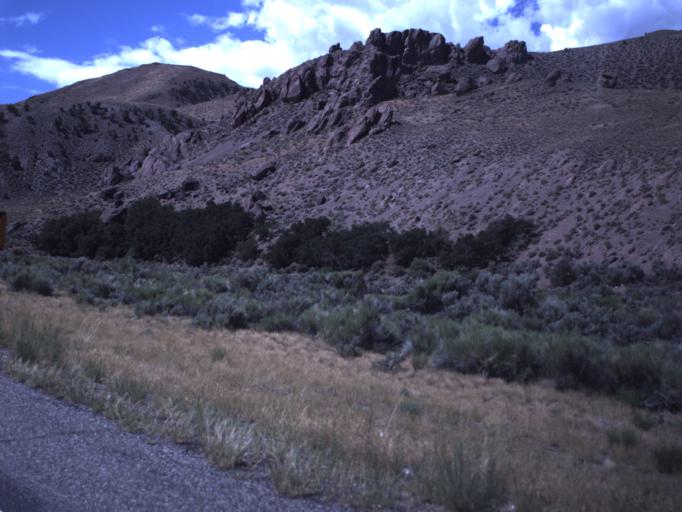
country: US
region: Utah
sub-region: Sevier County
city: Monroe
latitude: 38.4825
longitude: -112.2447
